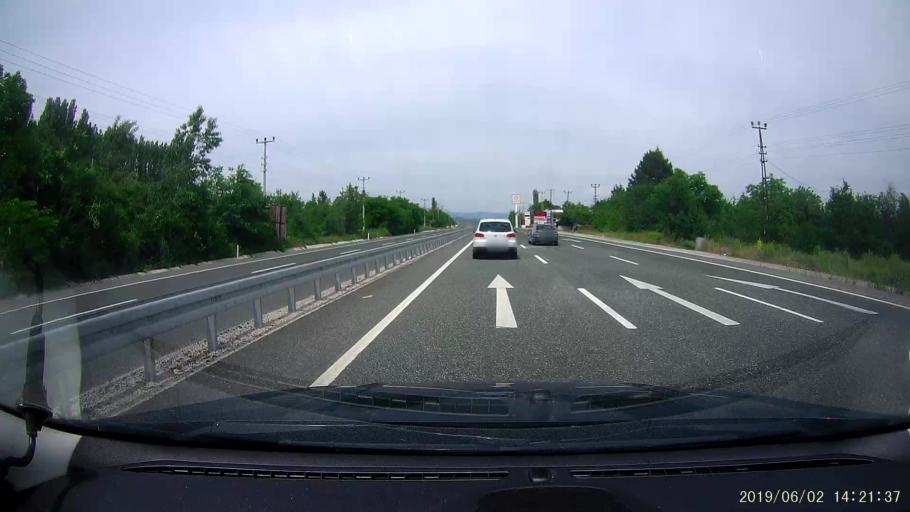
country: TR
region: Kastamonu
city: Tosya
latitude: 40.9808
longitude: 34.0043
